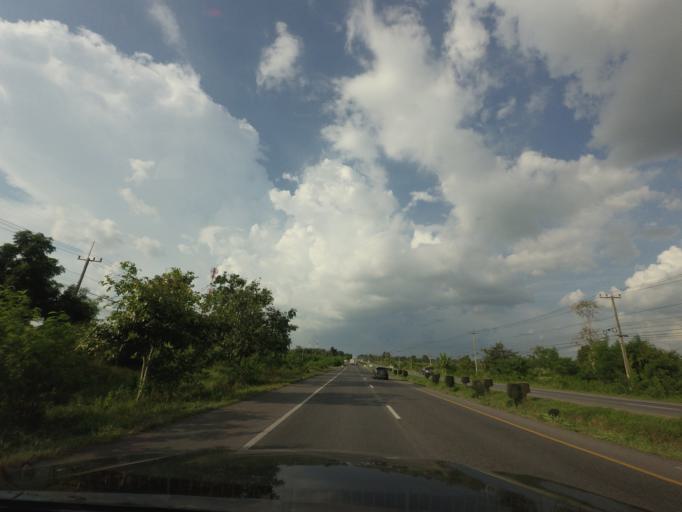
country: TH
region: Khon Kaen
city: Ban Haet
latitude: 16.2620
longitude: 102.7779
